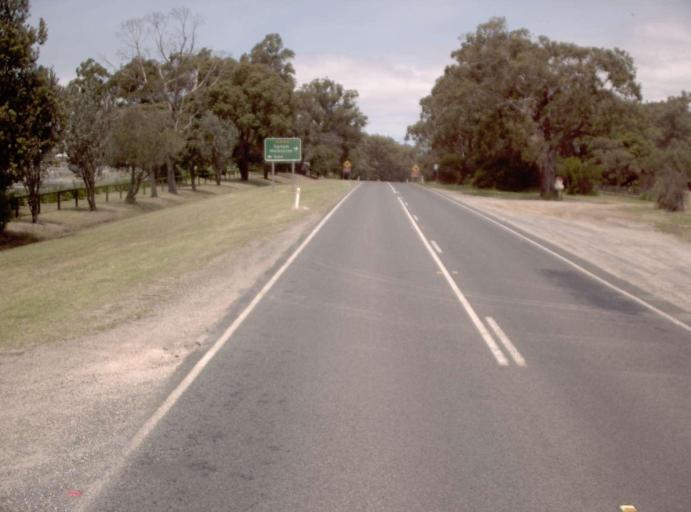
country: AU
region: Victoria
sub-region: Latrobe
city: Traralgon
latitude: -38.5427
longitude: 146.7022
